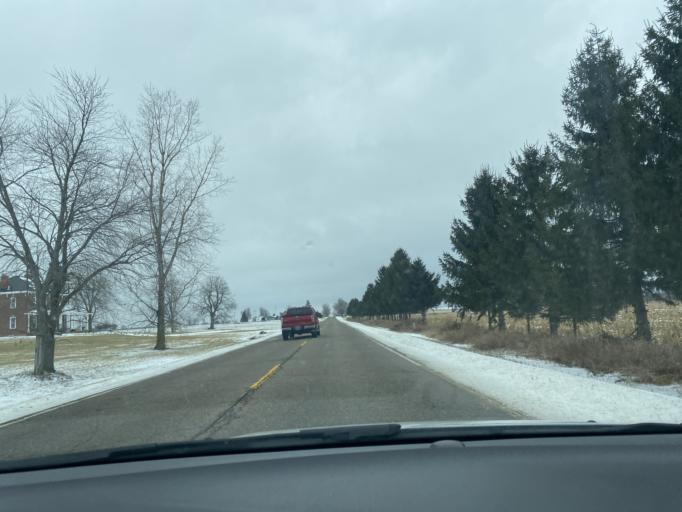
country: US
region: Michigan
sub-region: Lapeer County
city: North Branch
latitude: 43.2102
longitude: -83.0961
